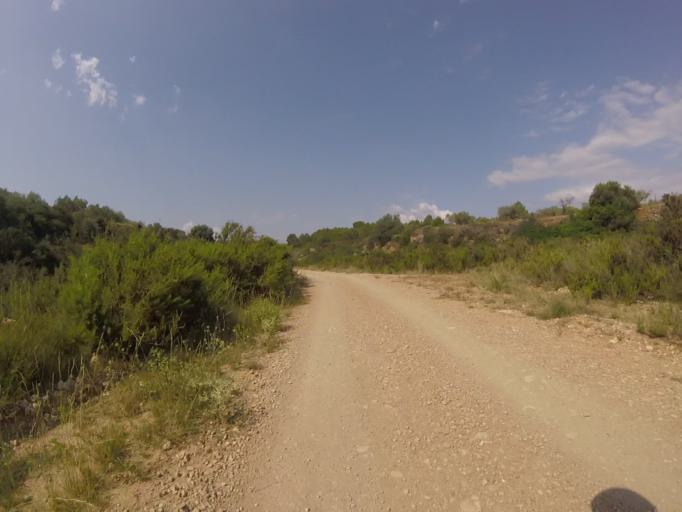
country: ES
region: Valencia
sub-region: Provincia de Castello
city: Cuevas de Vinroma
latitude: 40.3080
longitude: 0.1717
